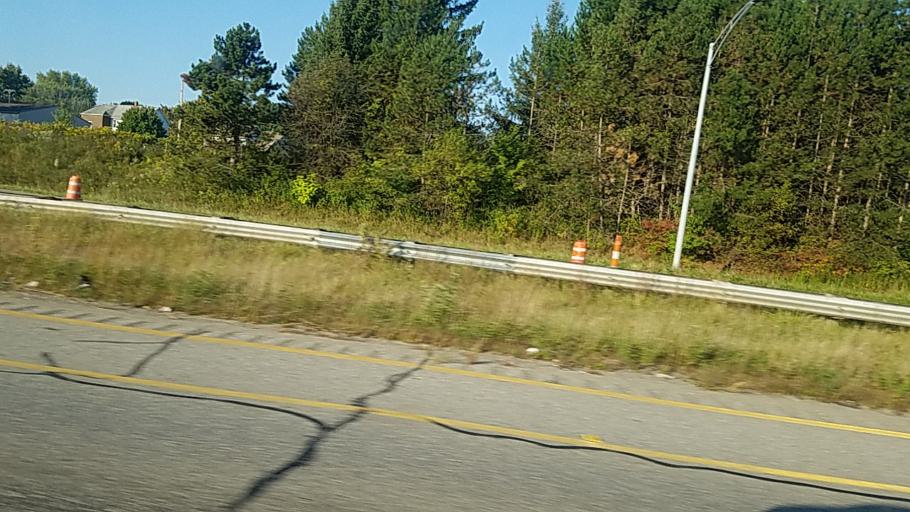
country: US
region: Ohio
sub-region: Trumbull County
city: Girard
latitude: 41.1165
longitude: -80.6930
